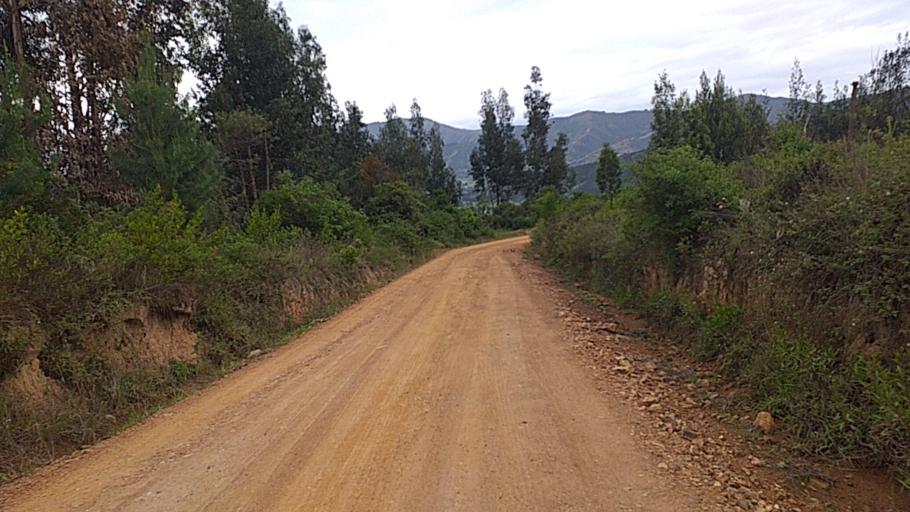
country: CO
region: Boyaca
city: Floresta
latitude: 5.8802
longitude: -72.9107
